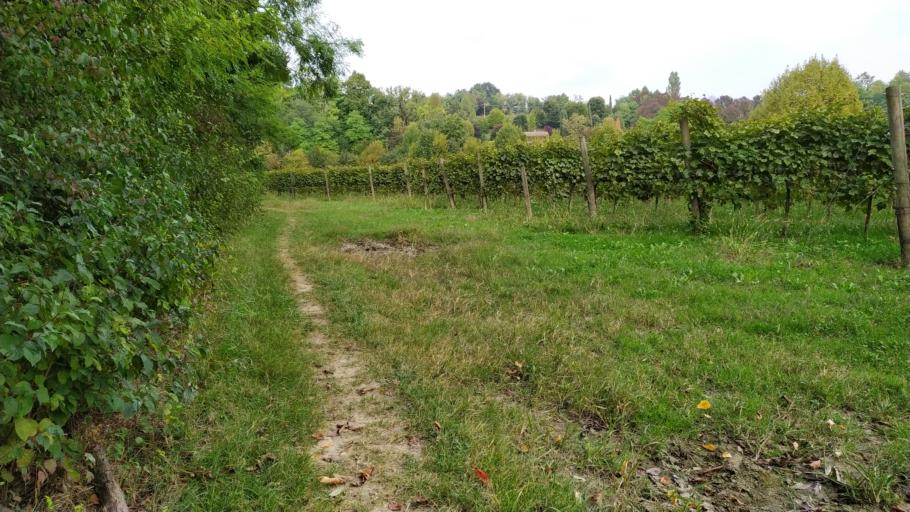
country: IT
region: Veneto
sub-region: Provincia di Treviso
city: Conegliano
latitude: 45.9046
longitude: 12.2946
